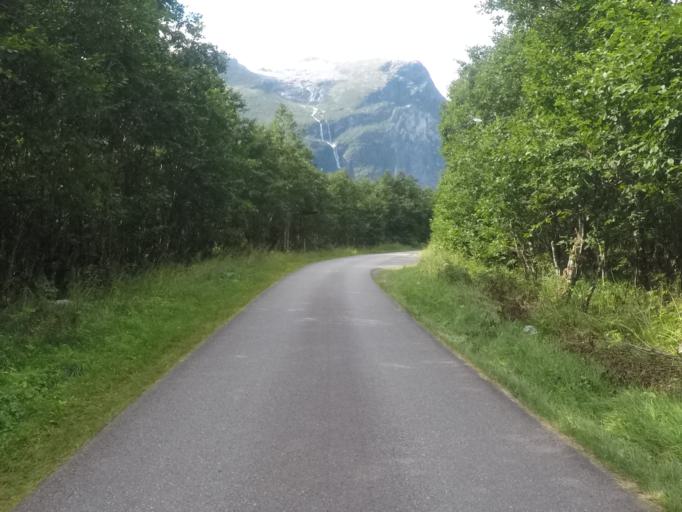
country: NO
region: Sogn og Fjordane
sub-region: Stryn
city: Stryn
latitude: 61.7732
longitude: 7.0245
